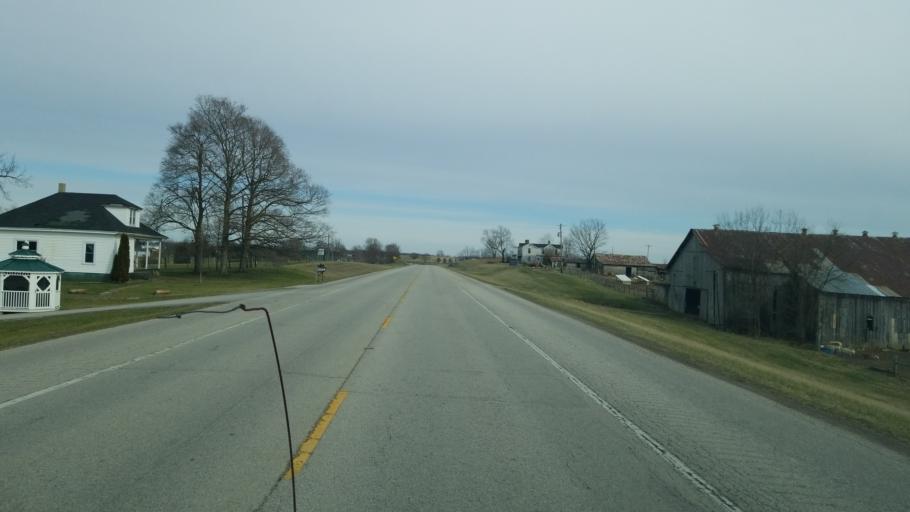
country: US
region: Kentucky
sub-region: Fleming County
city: Flemingsburg
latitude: 38.4837
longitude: -83.8674
